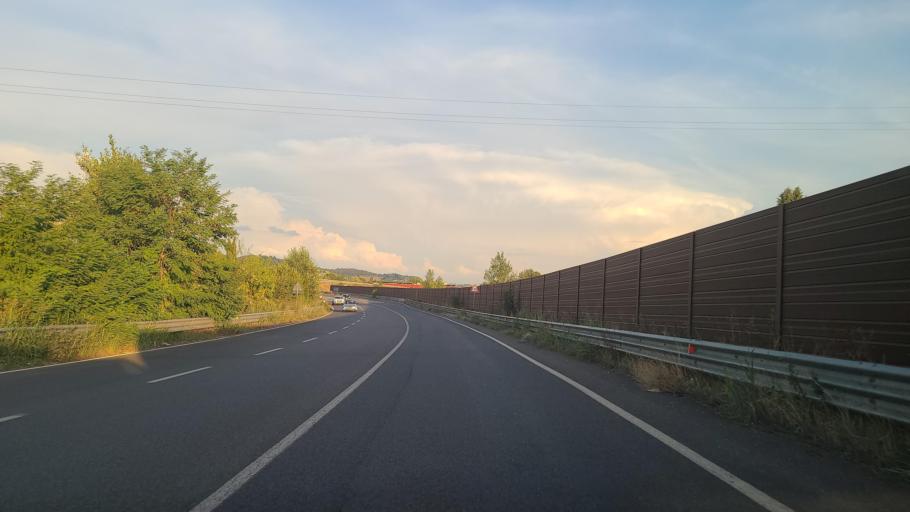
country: IT
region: Tuscany
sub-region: Provincia di Siena
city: Poggibonsi
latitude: 43.4833
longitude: 11.1215
